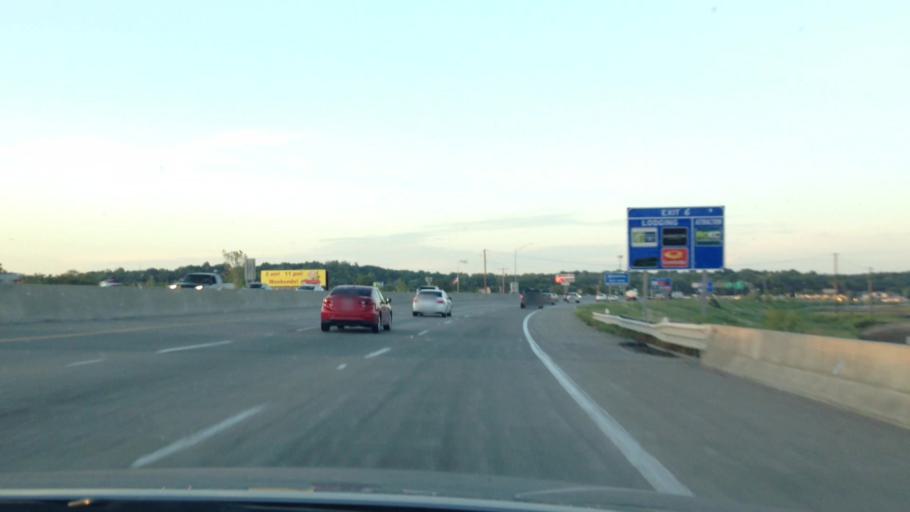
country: US
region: Missouri
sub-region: Clay County
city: North Kansas City
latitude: 39.1384
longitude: -94.5662
